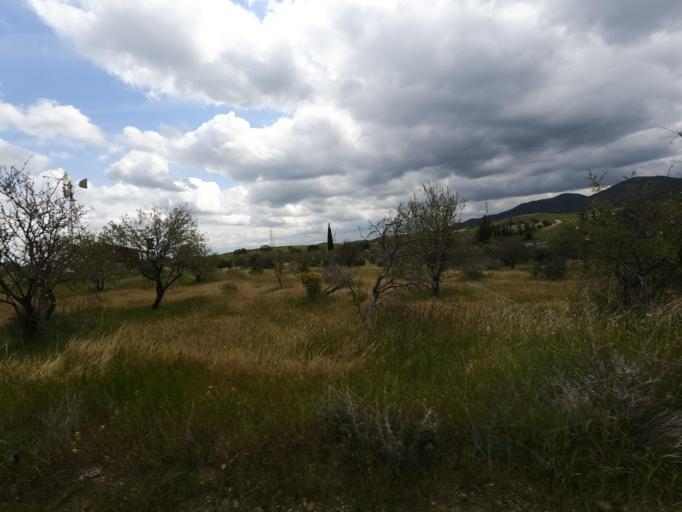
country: CY
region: Lefkosia
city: Astromeritis
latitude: 35.0879
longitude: 32.9584
